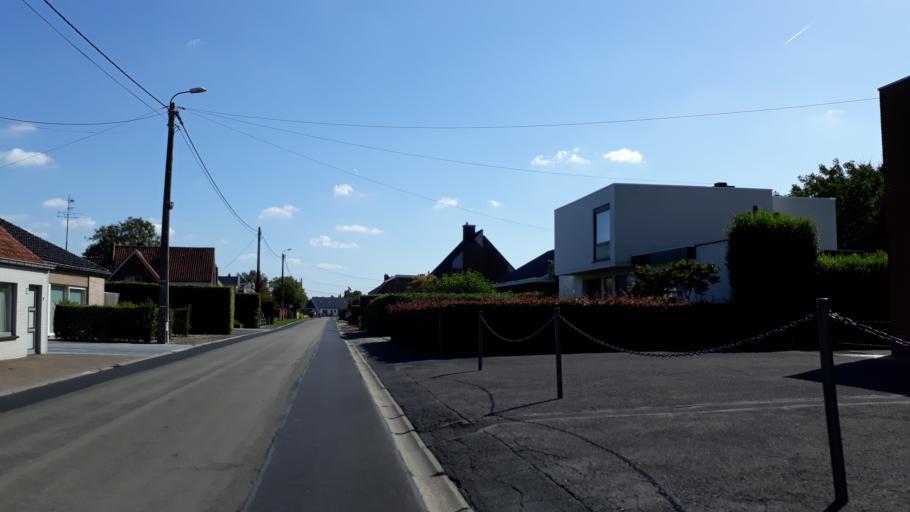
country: BE
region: Flanders
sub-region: Provincie West-Vlaanderen
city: Torhout
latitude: 51.0852
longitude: 3.1102
